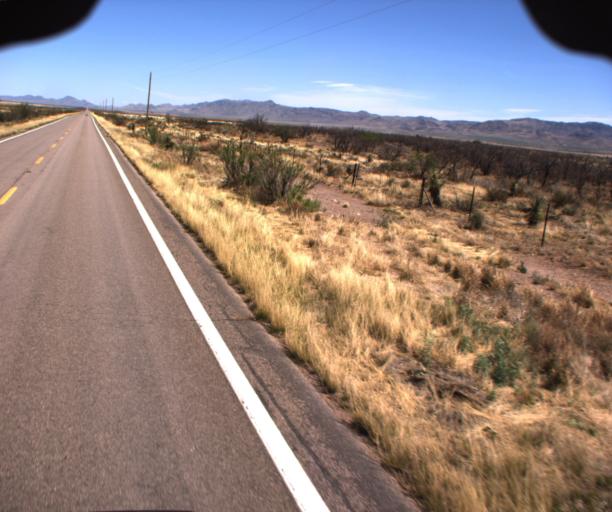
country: US
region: Arizona
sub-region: Cochise County
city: Douglas
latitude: 31.7011
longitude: -109.1255
